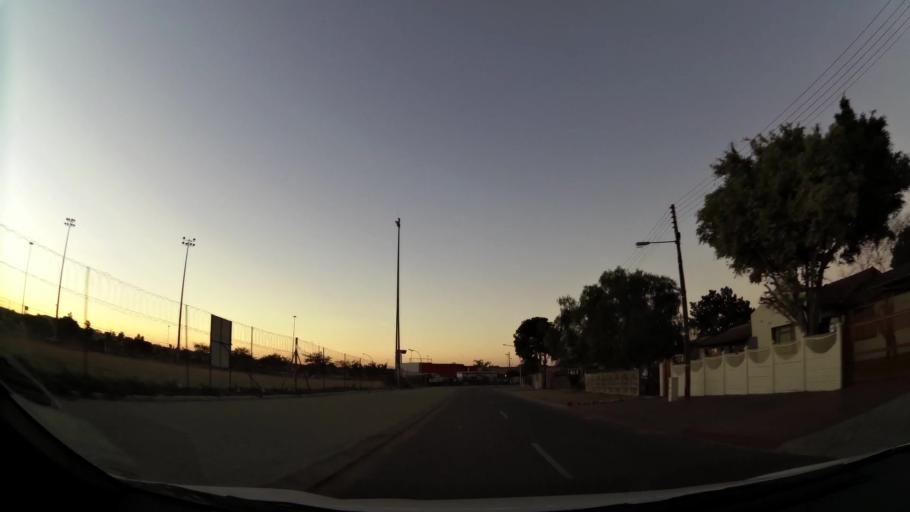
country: ZA
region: Limpopo
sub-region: Capricorn District Municipality
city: Polokwane
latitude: -23.8540
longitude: 29.3911
